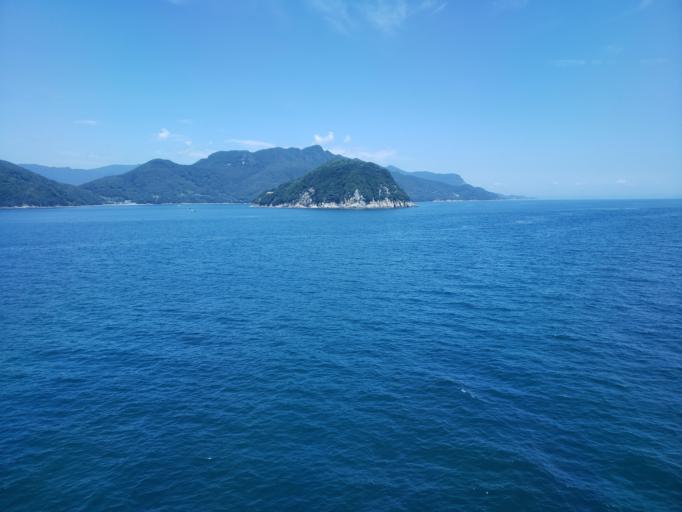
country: JP
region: Kagawa
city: Tonosho
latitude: 34.4280
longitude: 134.3517
